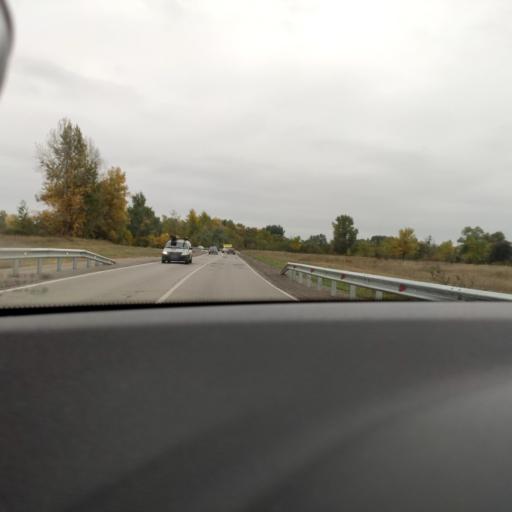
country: RU
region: Samara
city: Krasnyy Yar
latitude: 53.5010
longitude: 50.3558
